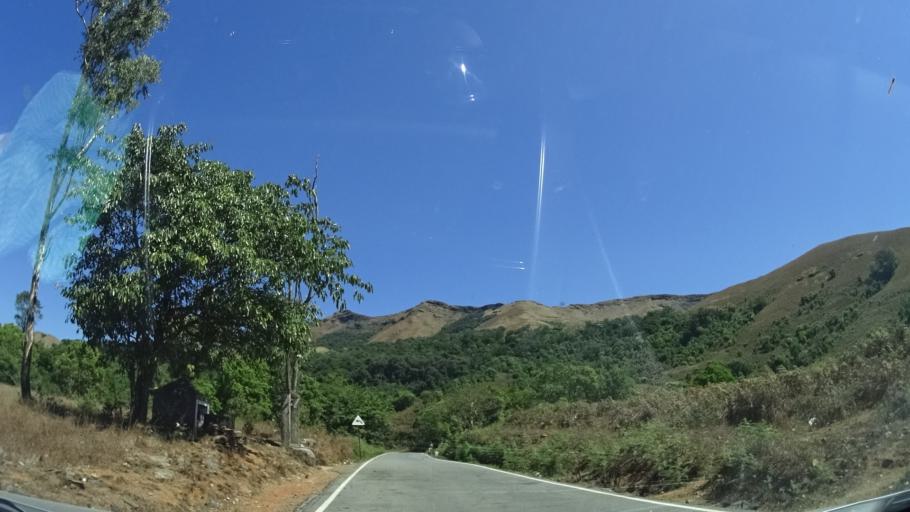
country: IN
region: Karnataka
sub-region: Udupi
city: Karkal
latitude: 13.2291
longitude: 75.1807
